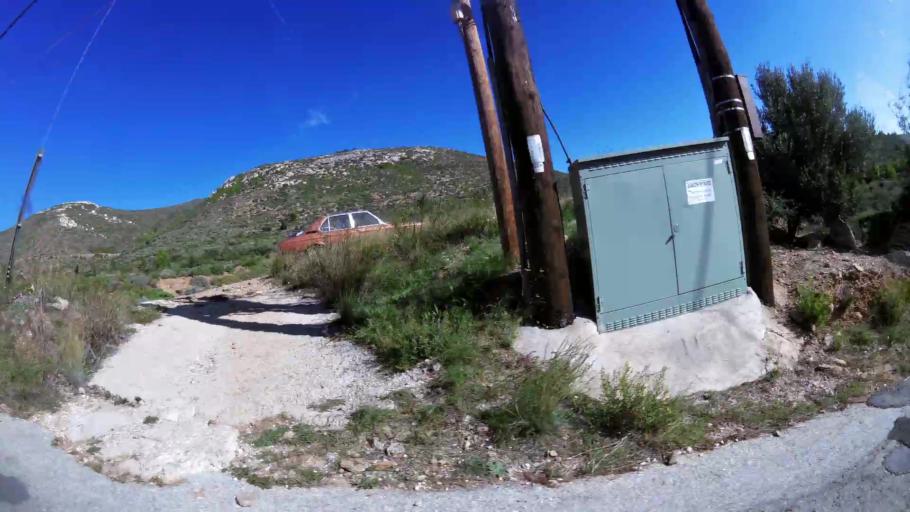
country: GR
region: Attica
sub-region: Nomarchia Anatolikis Attikis
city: Dioni
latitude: 38.0385
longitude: 23.9254
